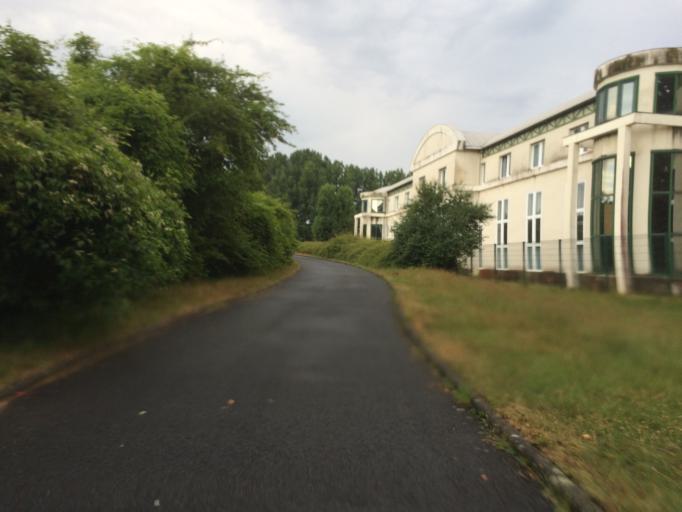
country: FR
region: Picardie
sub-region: Departement de l'Oise
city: Jaux
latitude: 49.3848
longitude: 2.7789
